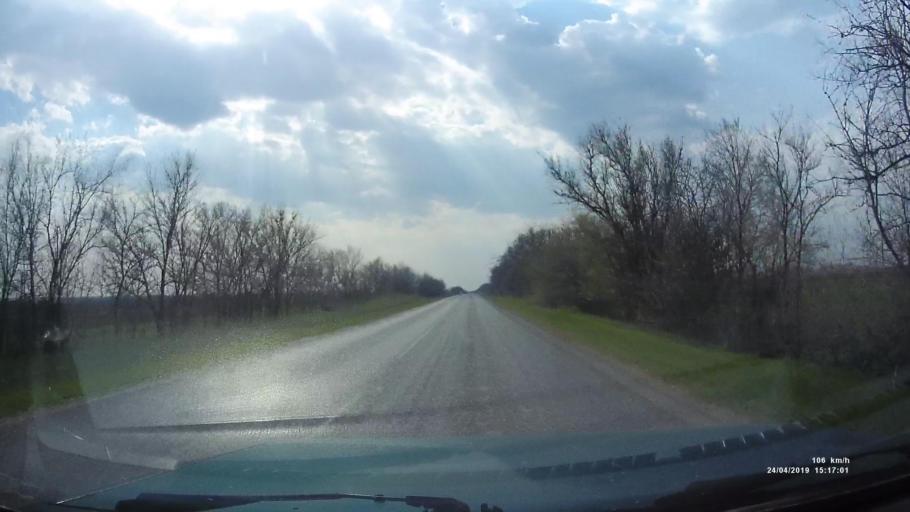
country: RU
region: Rostov
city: Remontnoye
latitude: 46.5465
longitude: 43.1994
